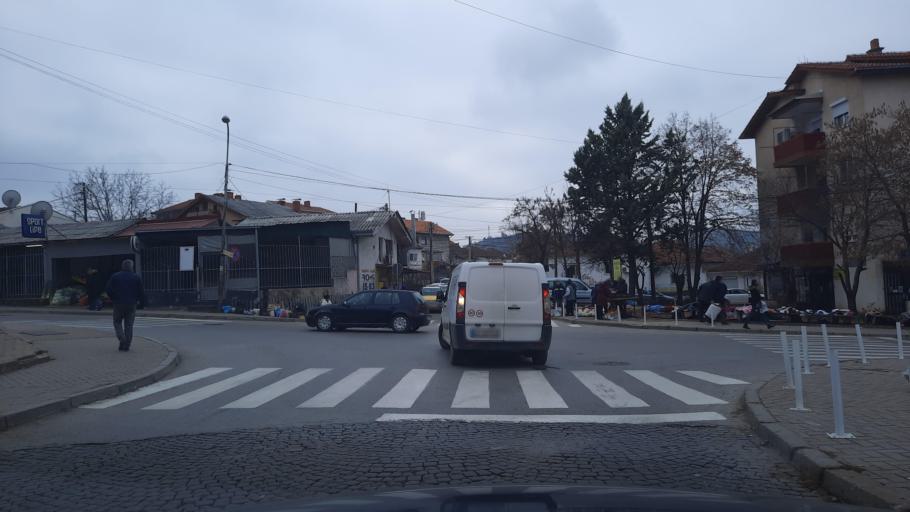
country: MK
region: Stip
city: Shtip
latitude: 41.7436
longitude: 22.1983
